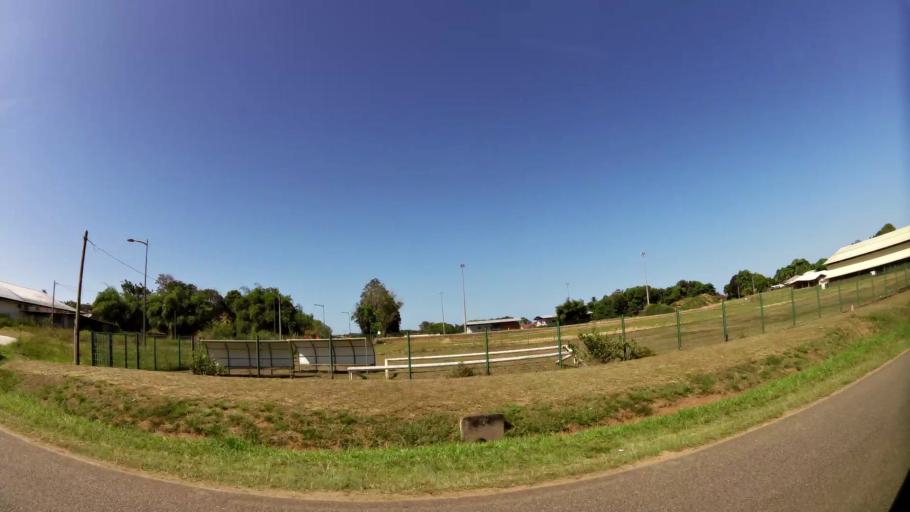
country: GF
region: Guyane
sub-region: Guyane
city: Remire-Montjoly
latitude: 4.9123
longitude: -52.2784
